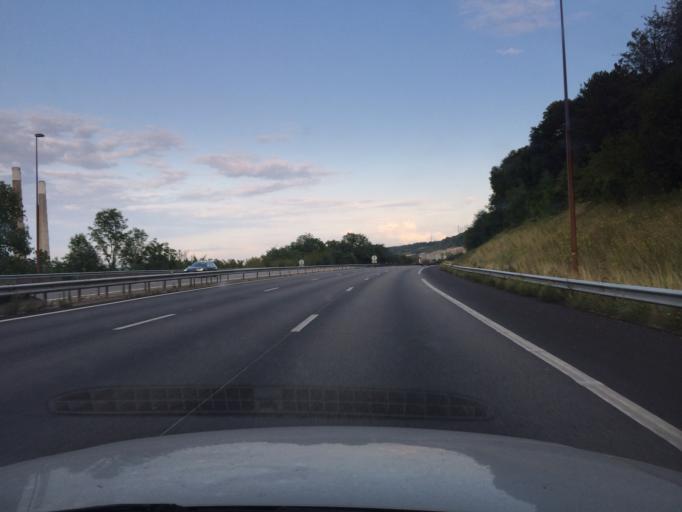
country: FR
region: Ile-de-France
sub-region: Departement des Yvelines
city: Guerville
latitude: 48.9683
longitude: 1.7432
